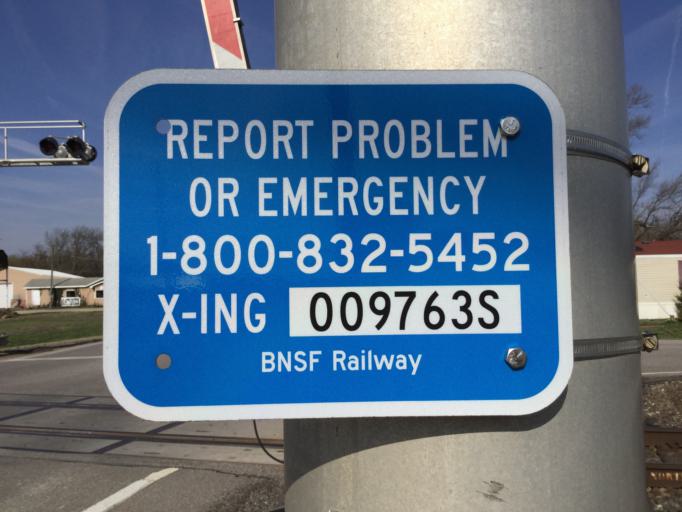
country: US
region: Kansas
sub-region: Butler County
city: Douglass
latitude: 37.5195
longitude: -97.0085
